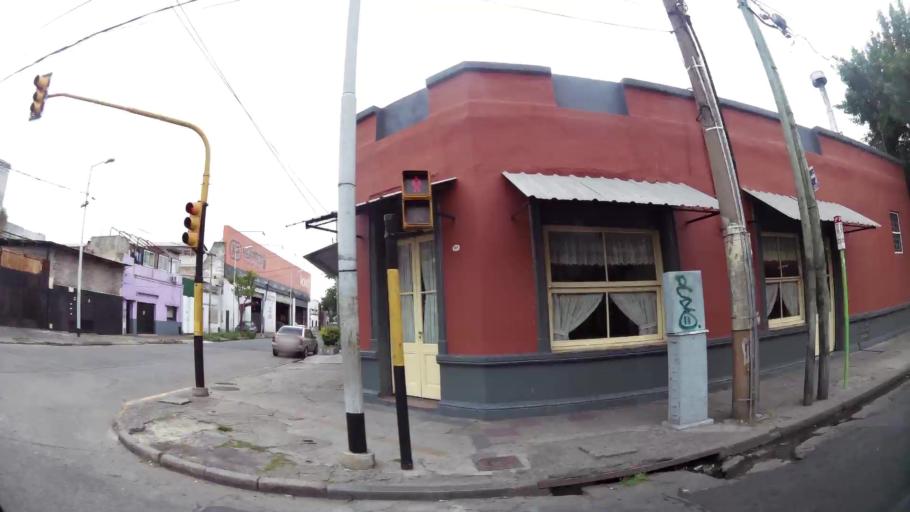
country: AR
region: Buenos Aires
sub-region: Partido de Avellaneda
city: Avellaneda
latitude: -34.6731
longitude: -58.3937
